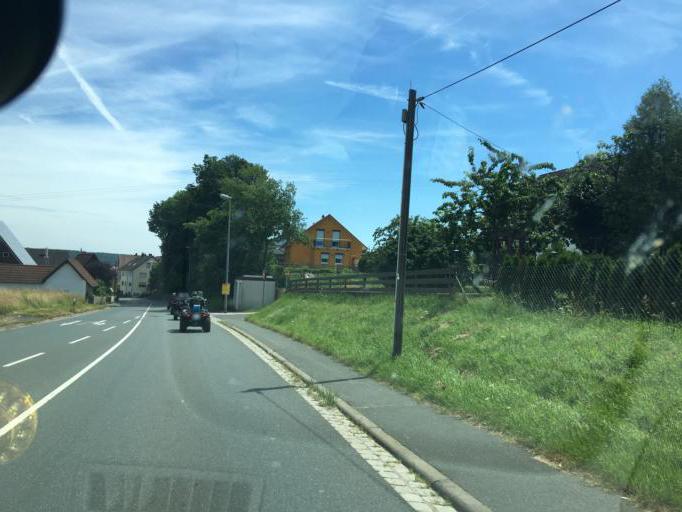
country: DE
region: Bavaria
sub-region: Upper Franconia
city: Heroldsbach
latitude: 49.7054
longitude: 10.9736
